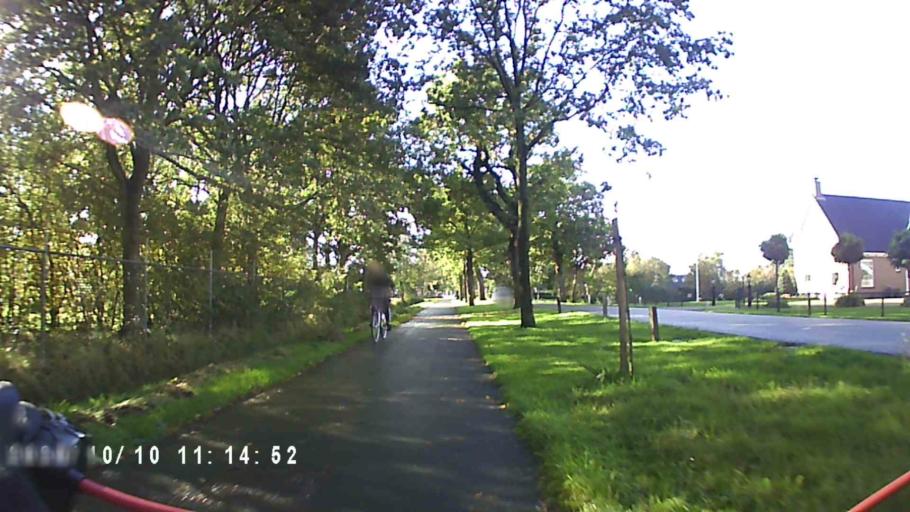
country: NL
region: Friesland
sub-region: Gemeente Smallingerland
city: Drachtstercompagnie
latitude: 53.1045
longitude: 6.2024
